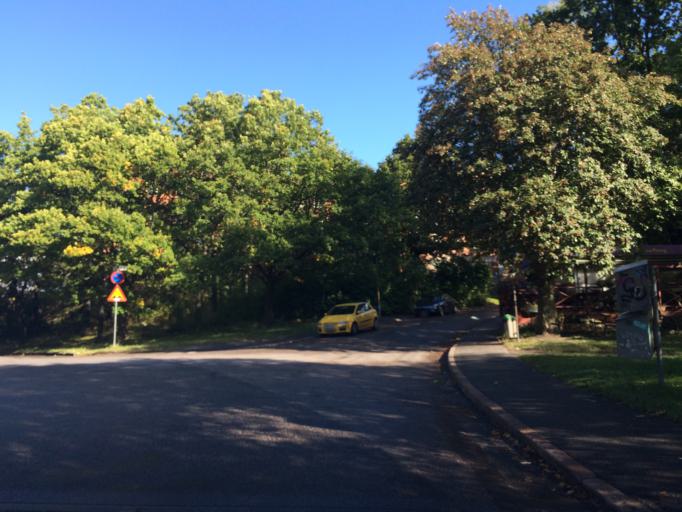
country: SE
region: Stockholm
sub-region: Stockholms Kommun
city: Arsta
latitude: 59.3037
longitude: 18.0033
